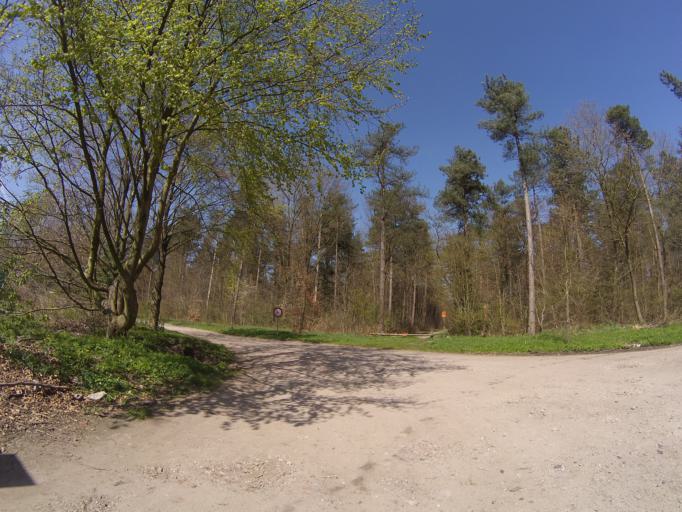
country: NL
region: Utrecht
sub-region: Gemeente Utrechtse Heuvelrug
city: Driebergen-Rijsenburg
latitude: 52.0821
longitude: 5.3164
